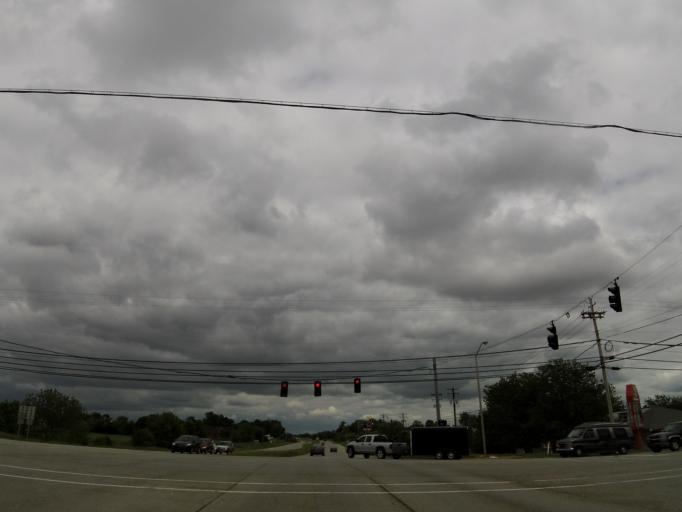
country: US
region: Kentucky
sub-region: Scott County
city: Georgetown
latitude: 38.1831
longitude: -84.5613
